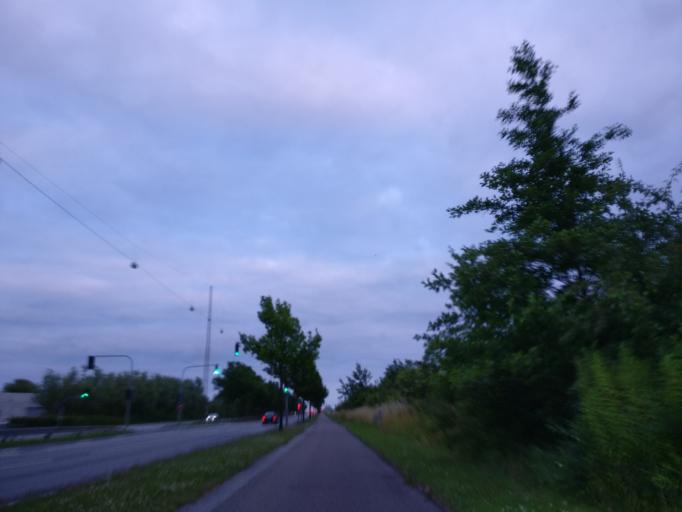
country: DK
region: Capital Region
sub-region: Hvidovre Kommune
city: Hvidovre
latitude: 55.6542
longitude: 12.4554
